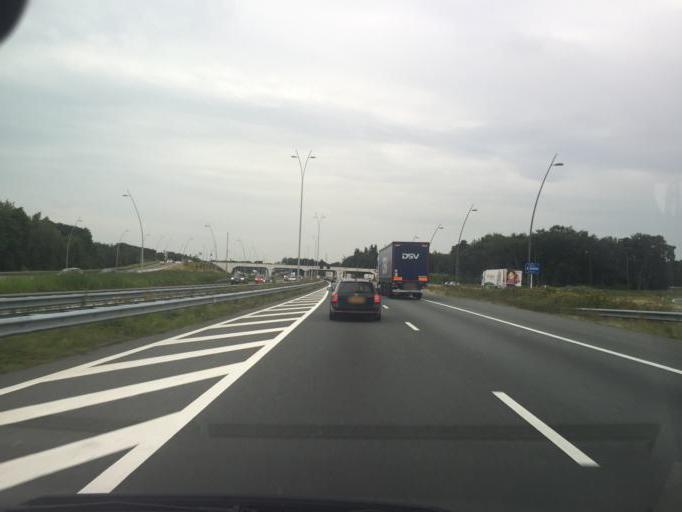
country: NL
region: North Brabant
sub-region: Gemeente Eindhoven
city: Meerhoven
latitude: 51.4630
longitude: 5.4070
